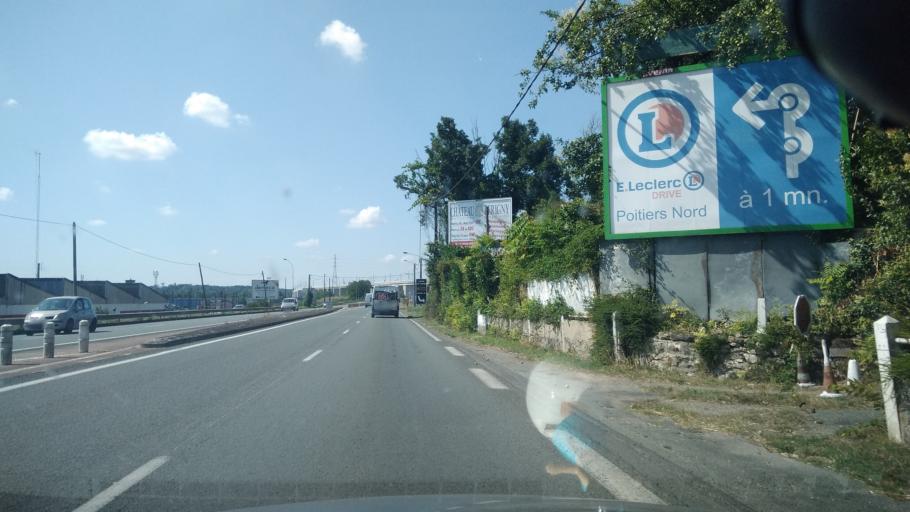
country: FR
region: Poitou-Charentes
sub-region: Departement de la Vienne
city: Chasseneuil-du-Poitou
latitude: 46.6270
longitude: 0.3548
